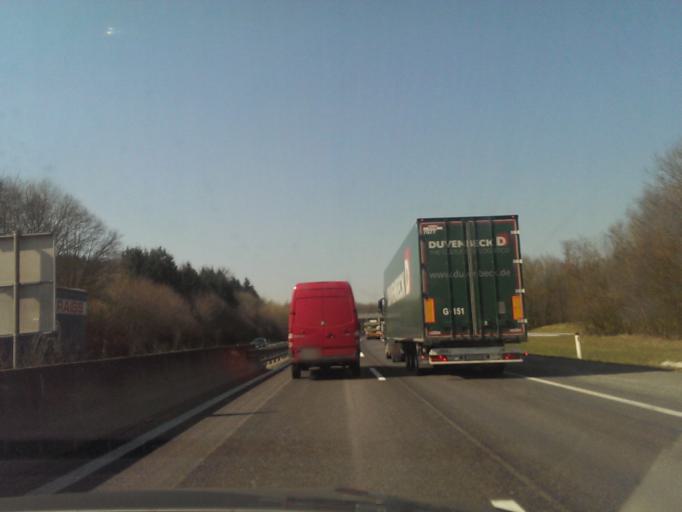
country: AT
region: Upper Austria
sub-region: Politischer Bezirk Ried im Innkreis
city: Ried im Innkreis
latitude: 48.2461
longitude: 13.5255
